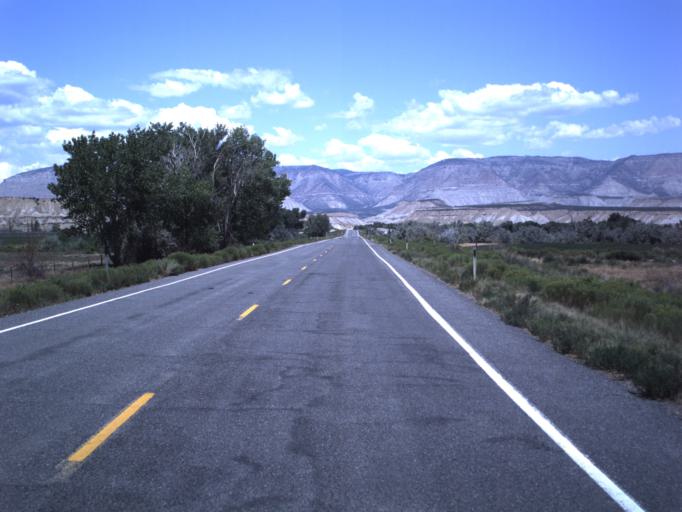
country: US
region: Utah
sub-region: Emery County
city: Orangeville
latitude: 39.2191
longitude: -111.0680
